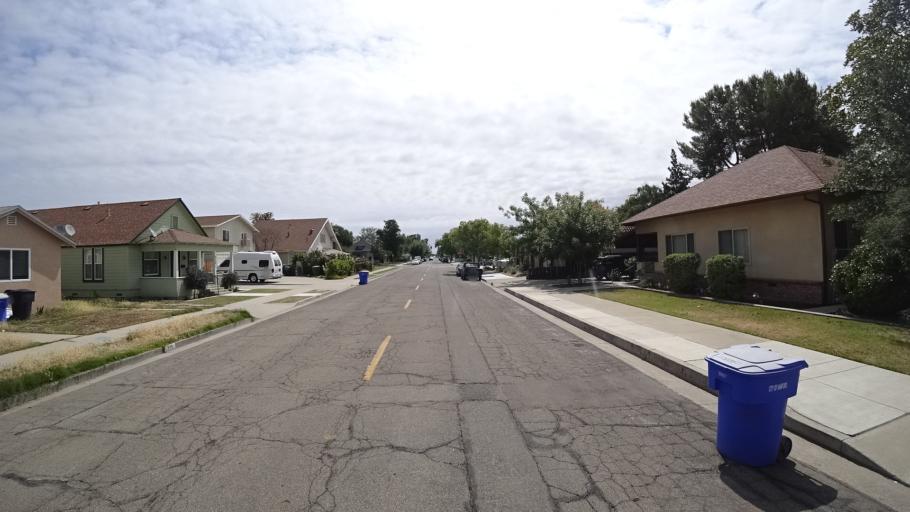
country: US
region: California
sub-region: Kings County
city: Hanford
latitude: 36.3340
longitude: -119.6486
